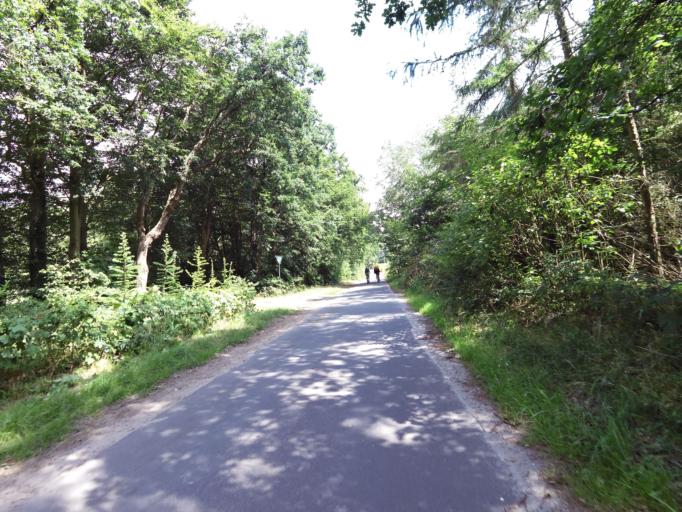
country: DE
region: Lower Saxony
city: Nordholz
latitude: 53.8364
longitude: 8.5838
